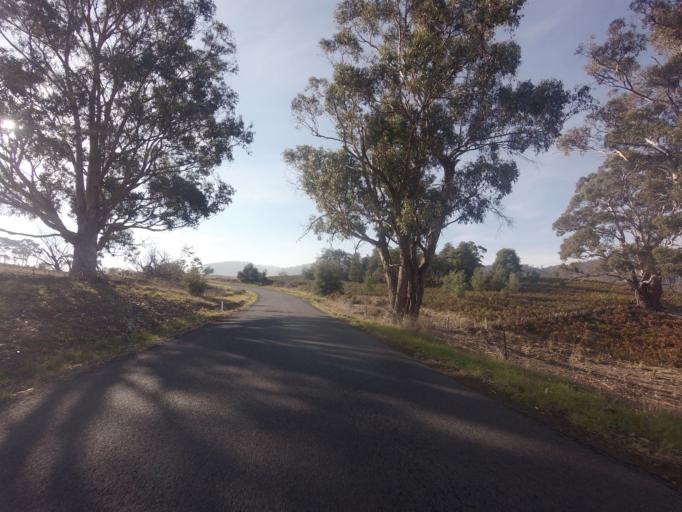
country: AU
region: Tasmania
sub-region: Brighton
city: Bridgewater
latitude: -42.5142
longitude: 147.4070
